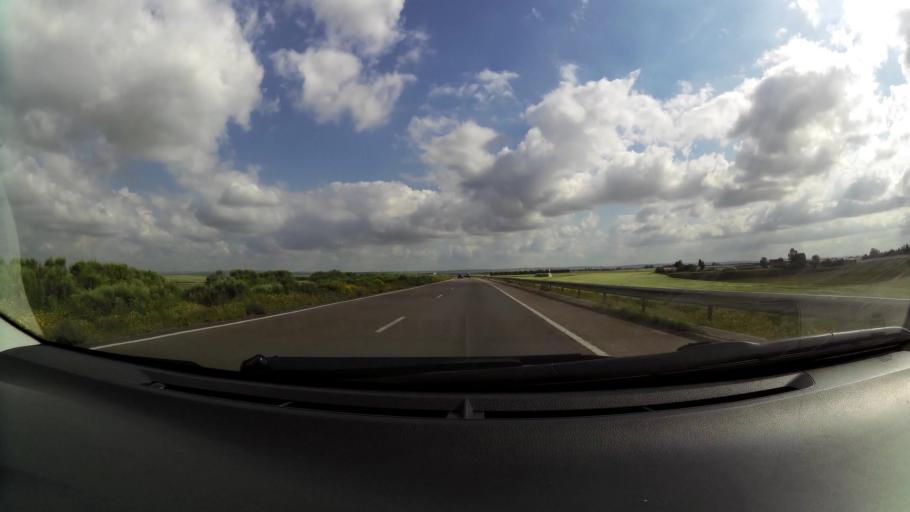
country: MA
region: Chaouia-Ouardigha
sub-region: Settat Province
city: Berrechid
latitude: 33.1953
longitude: -7.5760
